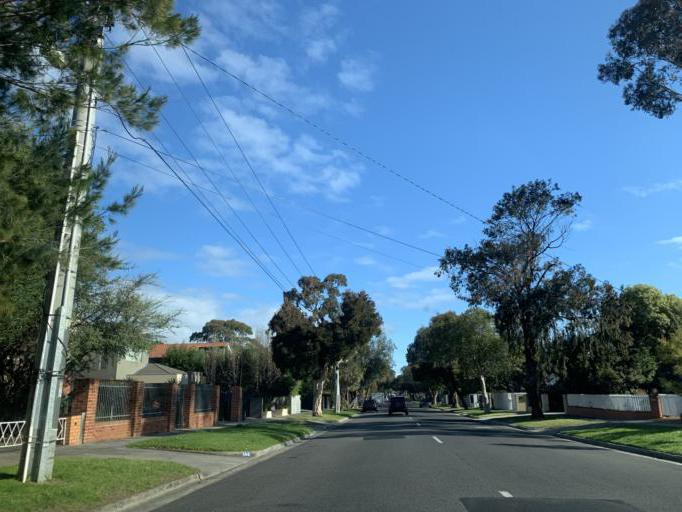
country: AU
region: Victoria
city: Beaumaris
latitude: -37.9838
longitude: 145.0440
